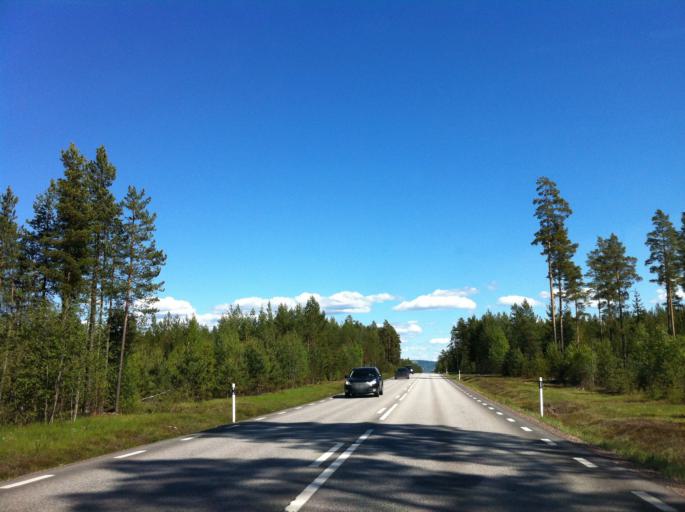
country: SE
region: Dalarna
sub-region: Rattviks Kommun
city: Vikarbyn
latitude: 60.9090
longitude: 14.9189
